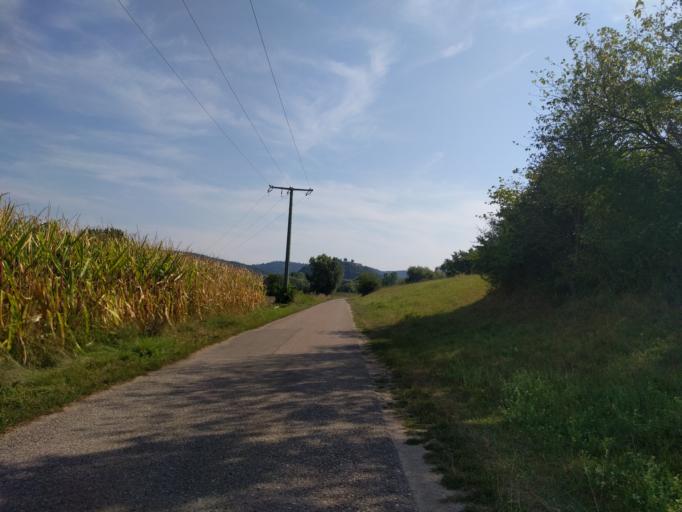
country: DE
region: Bavaria
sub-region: Upper Palatinate
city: Tegernheim
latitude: 49.0239
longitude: 12.1905
